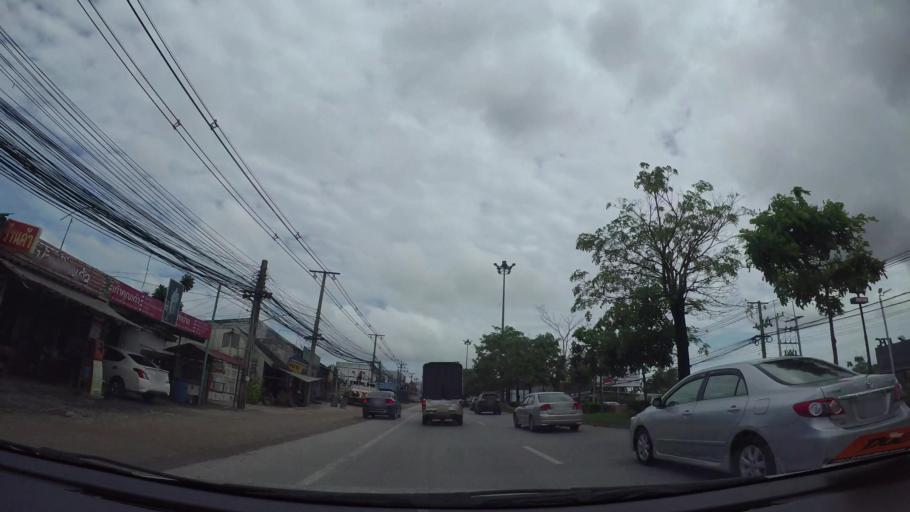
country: TH
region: Rayong
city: Rayong
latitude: 12.7014
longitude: 101.1883
